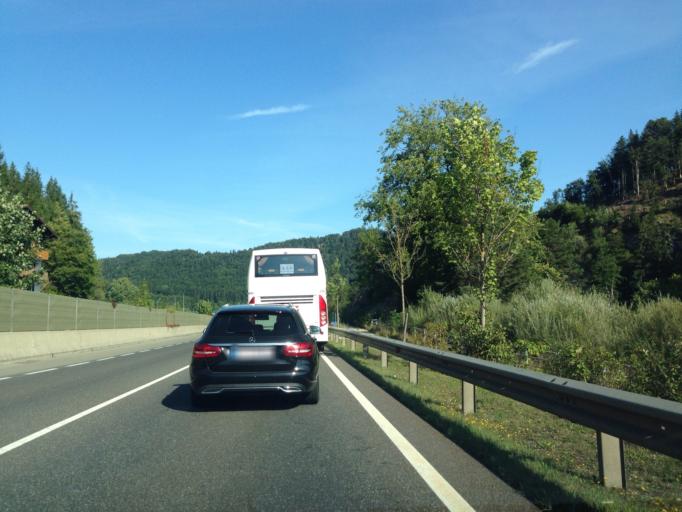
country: AT
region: Tyrol
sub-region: Politischer Bezirk Reutte
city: Musau
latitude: 47.5450
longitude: 10.6628
